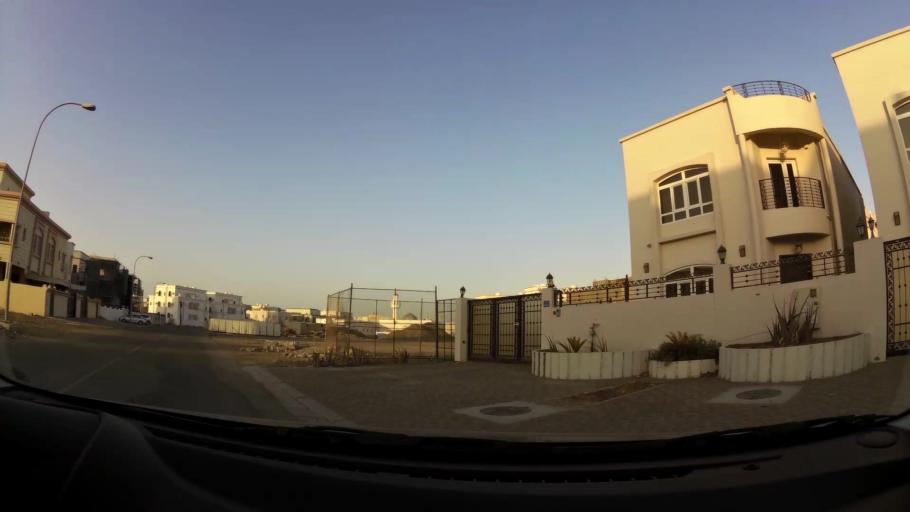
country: OM
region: Muhafazat Masqat
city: As Sib al Jadidah
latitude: 23.6115
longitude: 58.1991
